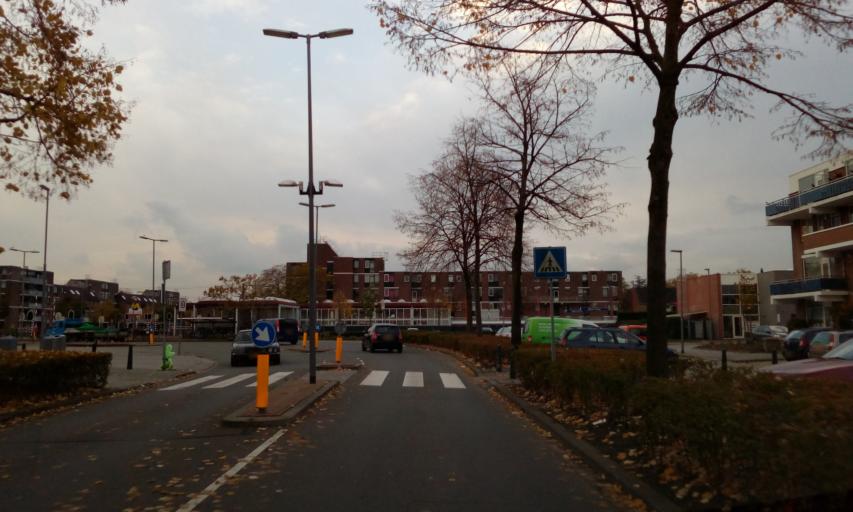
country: NL
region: South Holland
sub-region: Gemeente Capelle aan den IJssel
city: Capelle aan den IJssel
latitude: 51.9659
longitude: 4.5614
